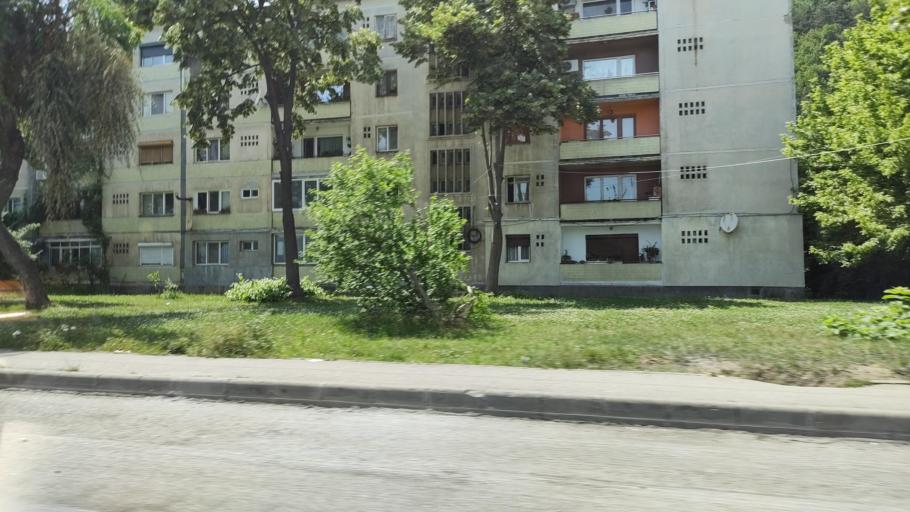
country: RO
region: Mehedinti
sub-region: Municipiul Orsova
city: Orsova
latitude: 44.7311
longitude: 22.4026
